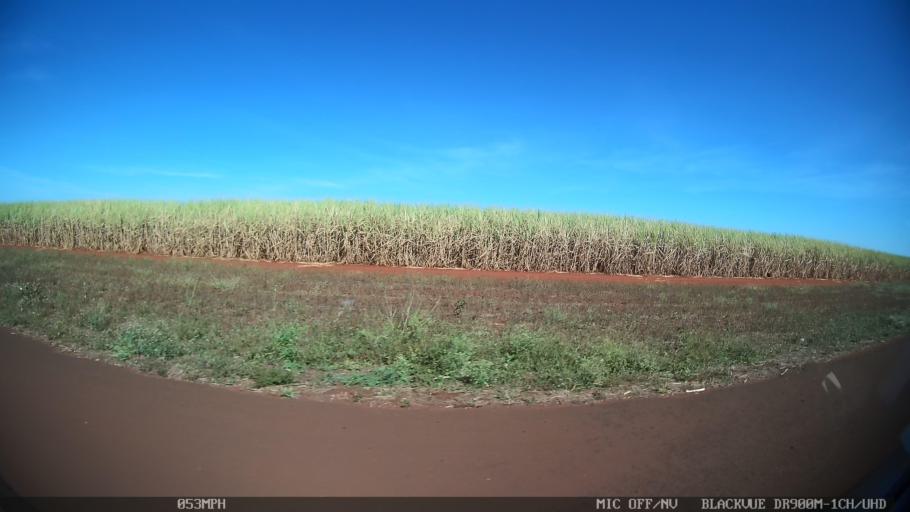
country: BR
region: Sao Paulo
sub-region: Guaira
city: Guaira
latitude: -20.4445
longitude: -48.2737
